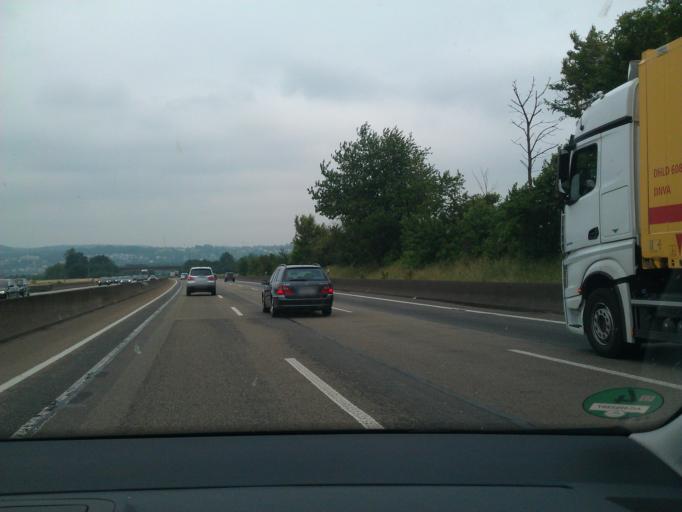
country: DE
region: Rheinland-Pfalz
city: Kaltenengers
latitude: 50.3974
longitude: 7.5556
